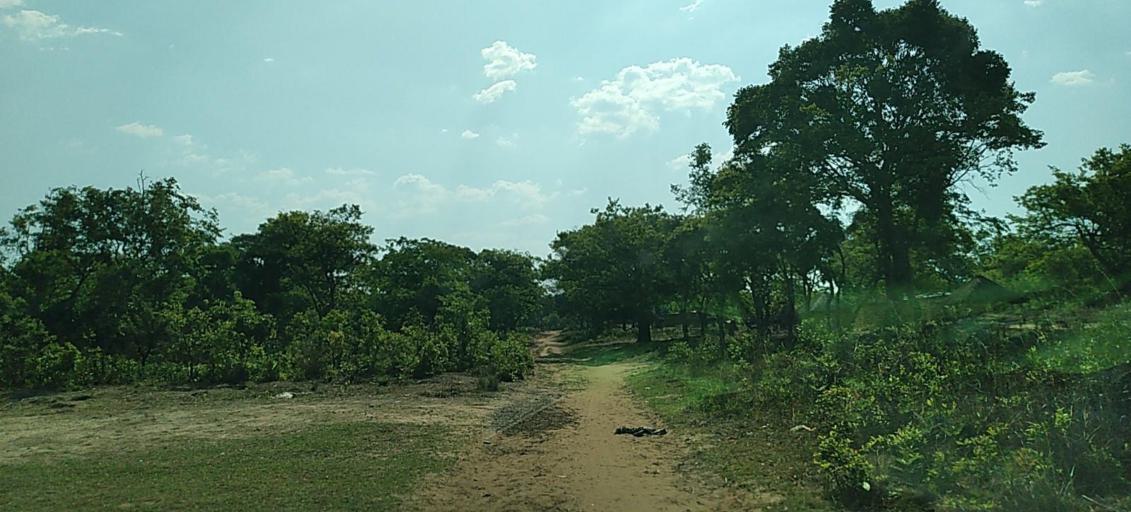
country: ZM
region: North-Western
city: Mwinilunga
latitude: -11.2977
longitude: 24.8579
